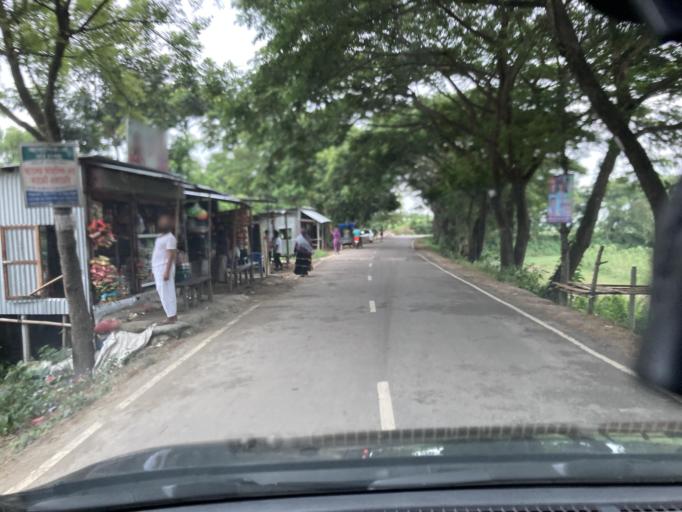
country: BD
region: Dhaka
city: Azimpur
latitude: 23.7717
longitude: 90.2048
